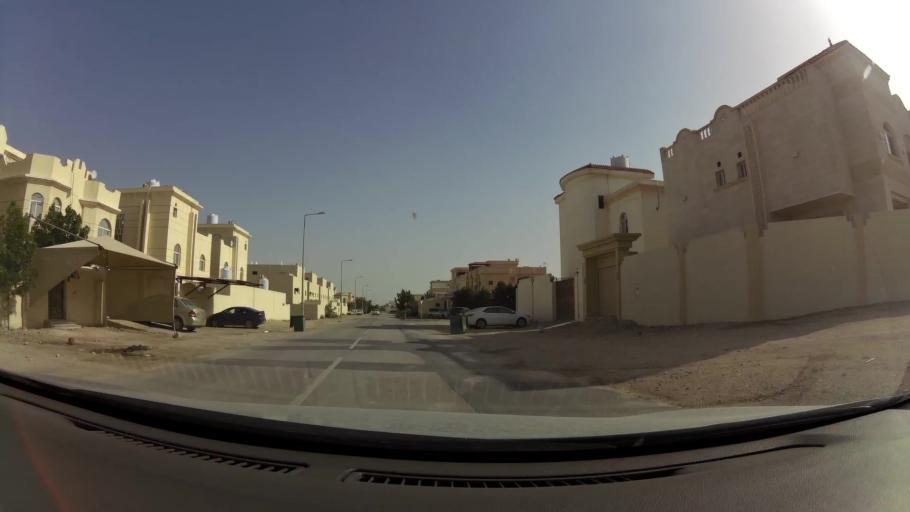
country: QA
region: Baladiyat ar Rayyan
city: Ar Rayyan
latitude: 25.3436
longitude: 51.4279
